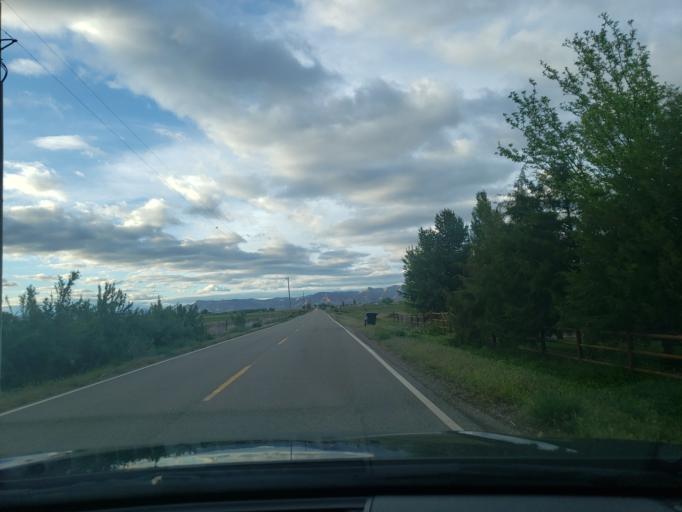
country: US
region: Colorado
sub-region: Mesa County
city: Fruita
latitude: 39.2186
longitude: -108.7197
